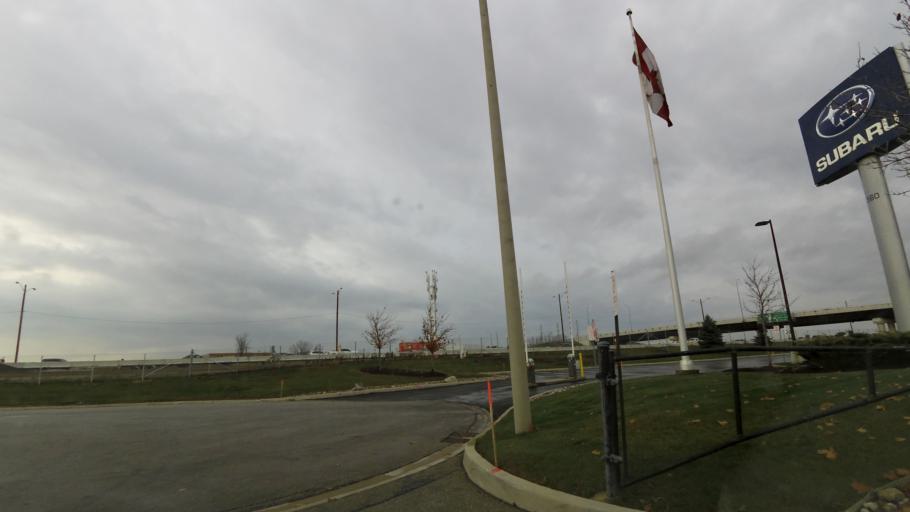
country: CA
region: Ontario
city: Mississauga
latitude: 43.6223
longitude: -79.7008
